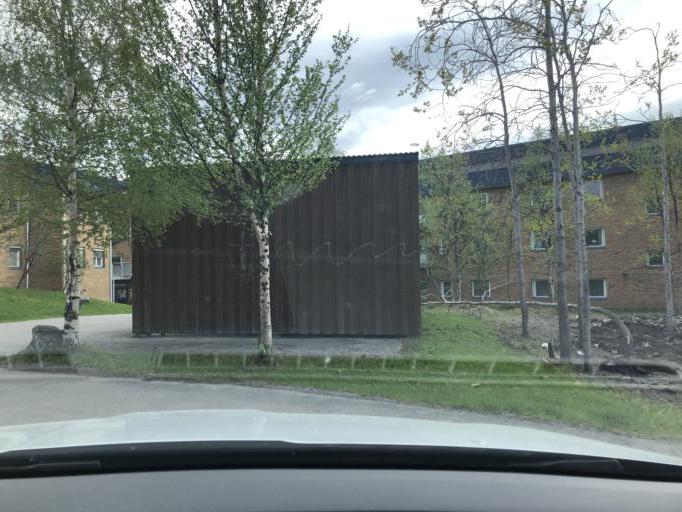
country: SE
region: Norrbotten
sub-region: Kiruna Kommun
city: Kiruna
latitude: 67.8494
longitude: 20.2358
